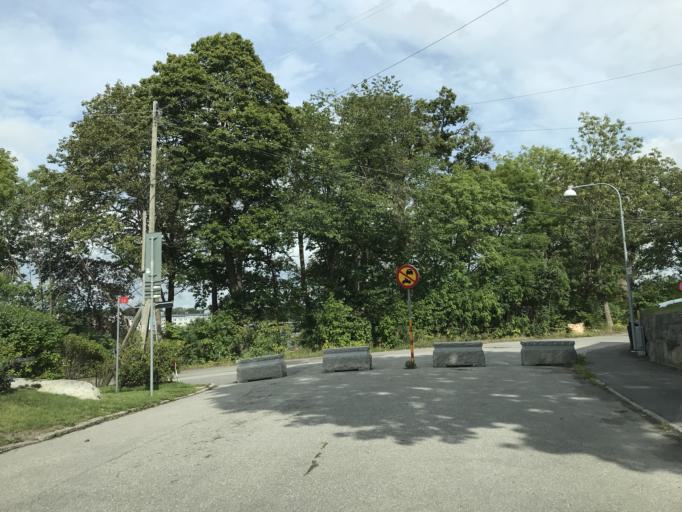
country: SE
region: Stockholm
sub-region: Sundbybergs Kommun
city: Sundbyberg
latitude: 59.3393
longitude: 17.9692
